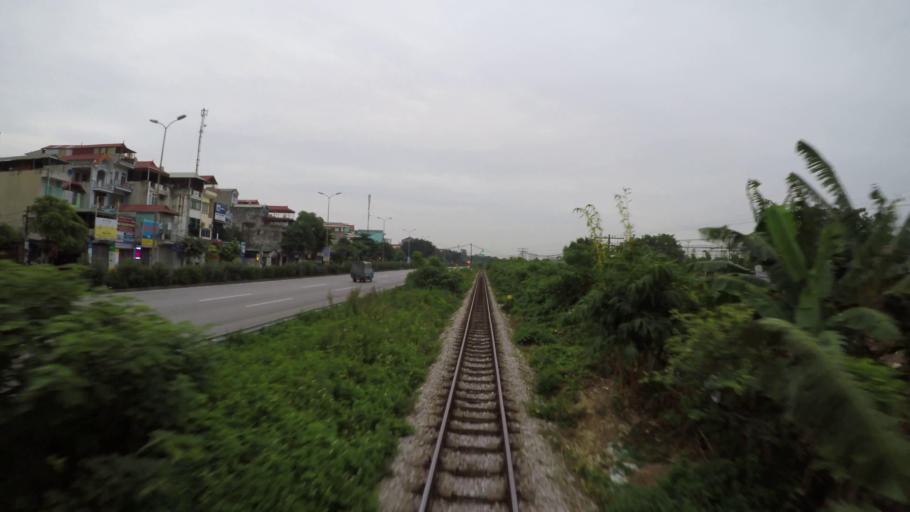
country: VN
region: Ha Noi
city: Trau Quy
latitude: 21.0118
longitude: 105.9510
